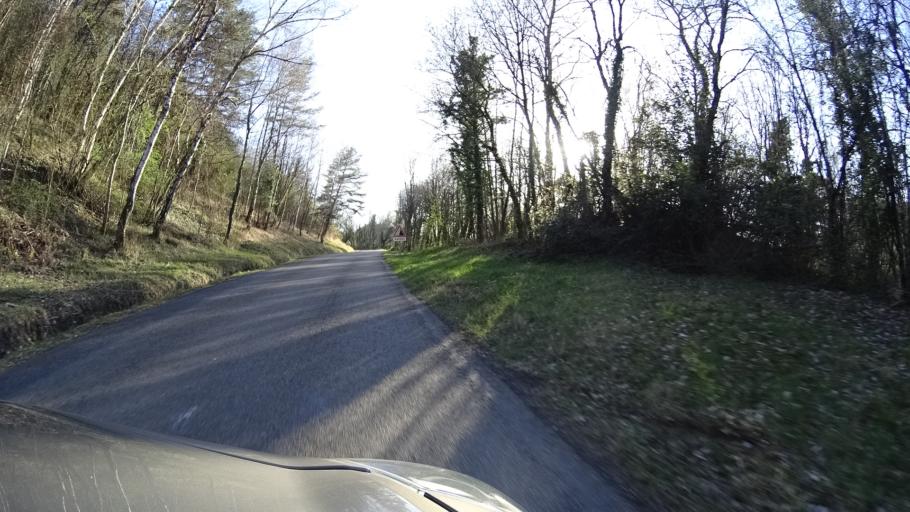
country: FR
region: Franche-Comte
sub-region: Departement du Doubs
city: Beure
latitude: 47.1990
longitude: 5.9927
